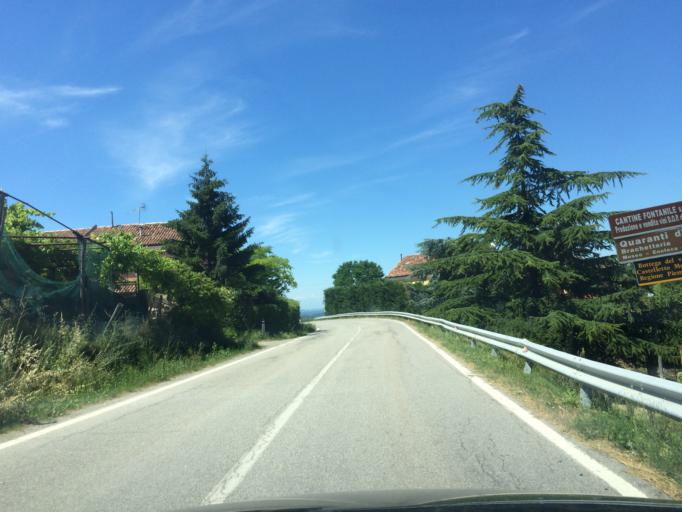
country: IT
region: Piedmont
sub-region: Provincia di Asti
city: Castel Boglione
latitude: 44.7302
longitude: 8.3968
